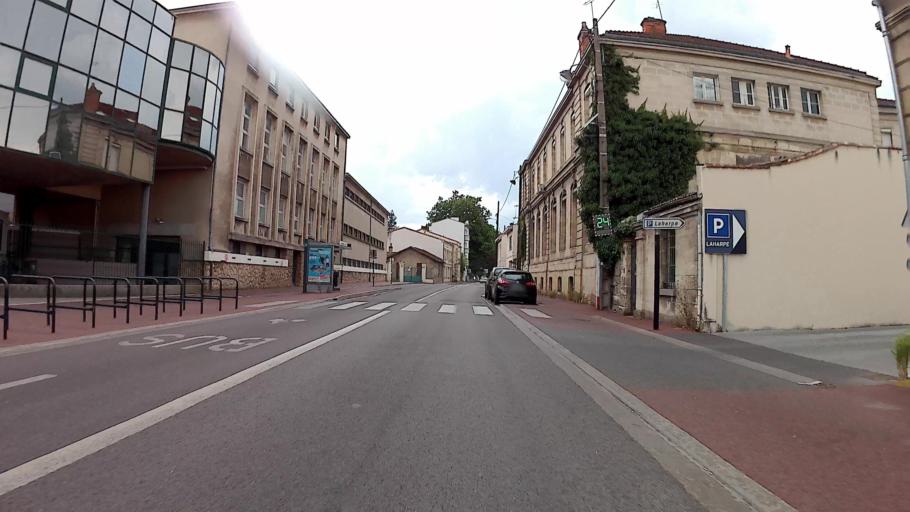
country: FR
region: Aquitaine
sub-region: Departement de la Gironde
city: Le Bouscat
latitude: 44.8539
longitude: -0.5968
